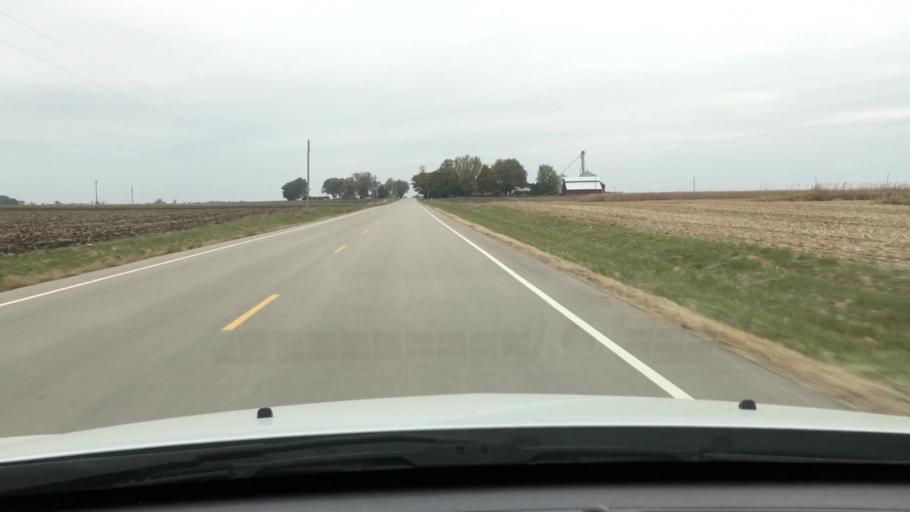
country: US
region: Illinois
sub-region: DeKalb County
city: Malta
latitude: 41.8167
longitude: -88.8864
